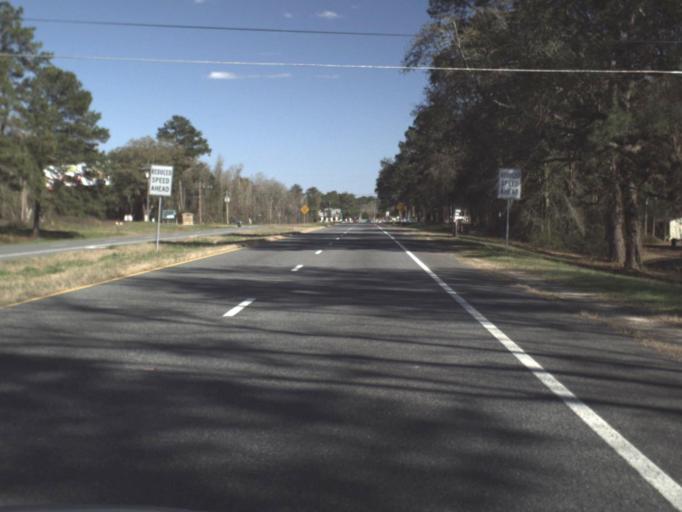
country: US
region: Florida
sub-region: Gadsden County
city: Midway
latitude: 30.4962
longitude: -84.4363
